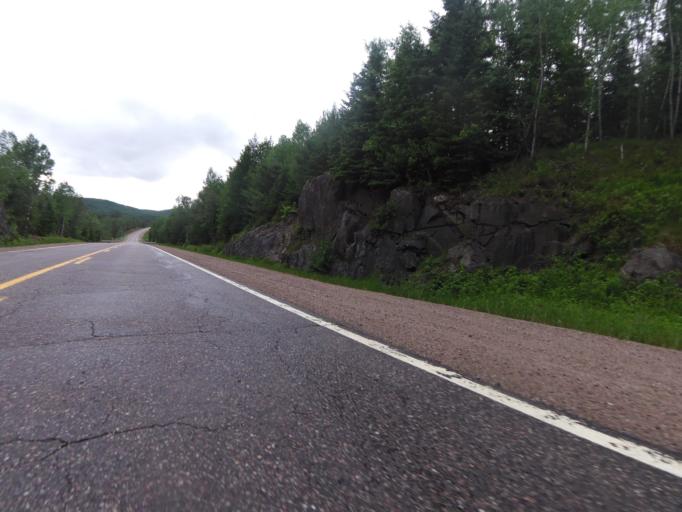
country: CA
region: Quebec
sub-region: Outaouais
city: Shawville
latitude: 45.9070
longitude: -76.2937
